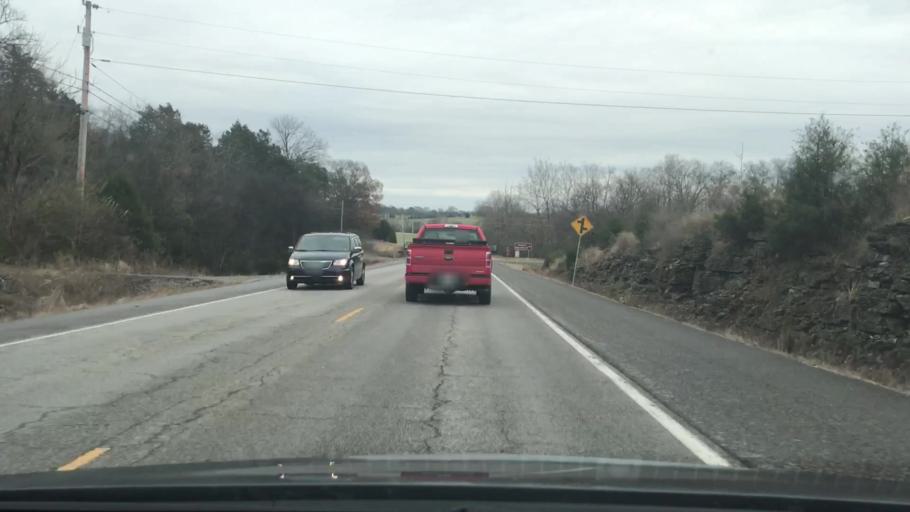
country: US
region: Tennessee
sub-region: Sumner County
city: Gallatin
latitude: 36.3968
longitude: -86.3200
